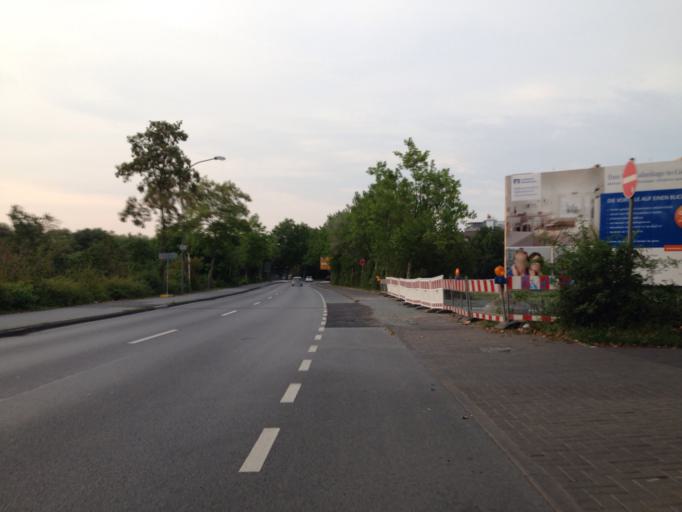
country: DE
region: Hesse
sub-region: Regierungsbezirk Giessen
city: Giessen
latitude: 50.5818
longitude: 8.6621
